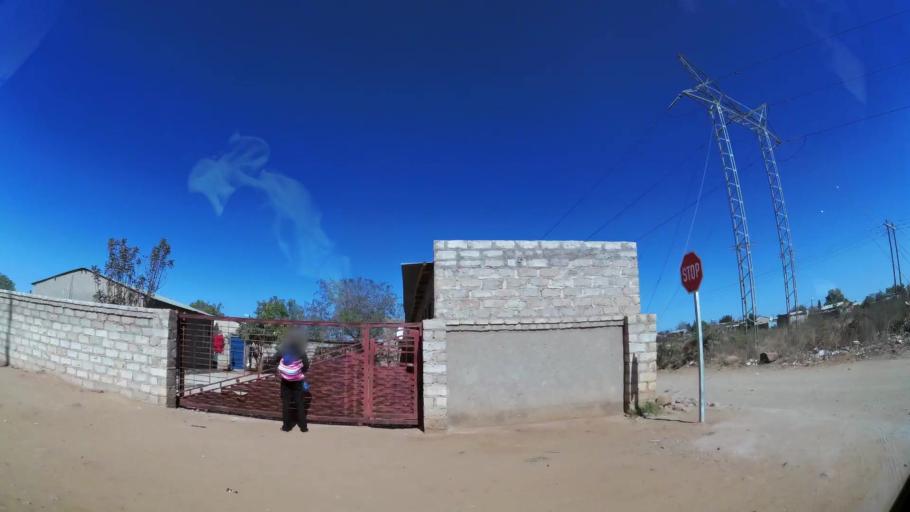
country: ZA
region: Limpopo
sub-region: Capricorn District Municipality
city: Polokwane
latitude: -23.8808
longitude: 29.4077
